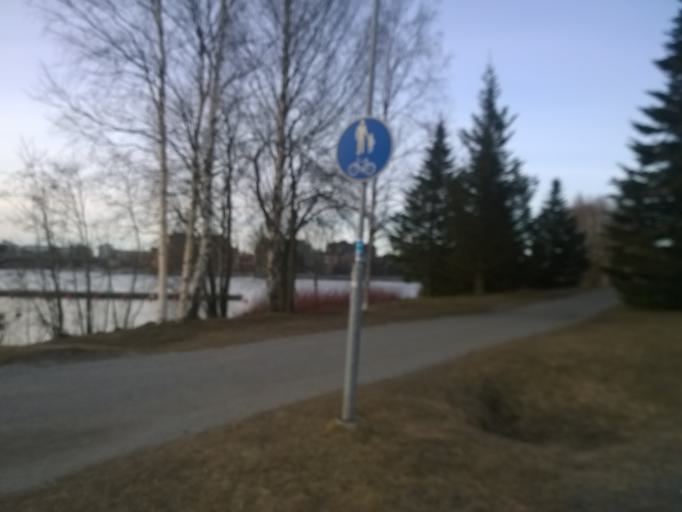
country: FI
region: Pirkanmaa
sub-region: Tampere
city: Tampere
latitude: 61.4866
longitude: 23.7609
